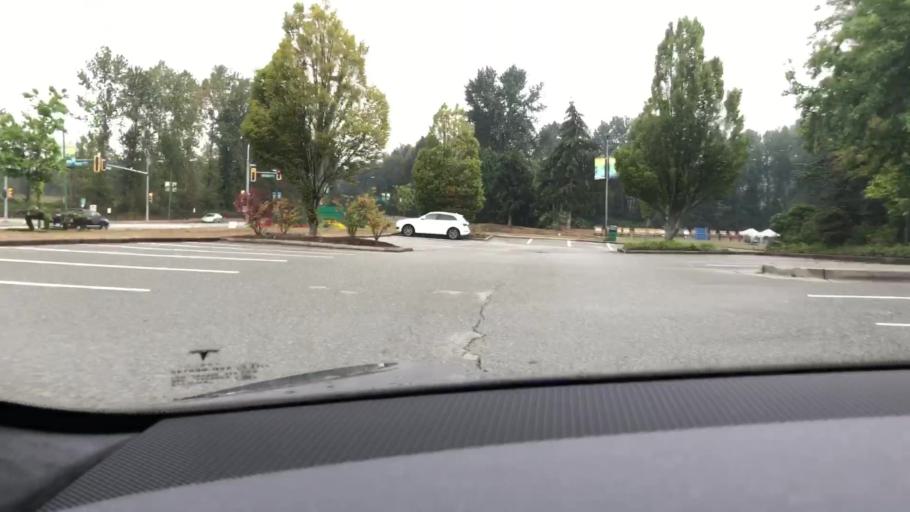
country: CA
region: British Columbia
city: Burnaby
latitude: 49.2526
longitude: -122.9659
